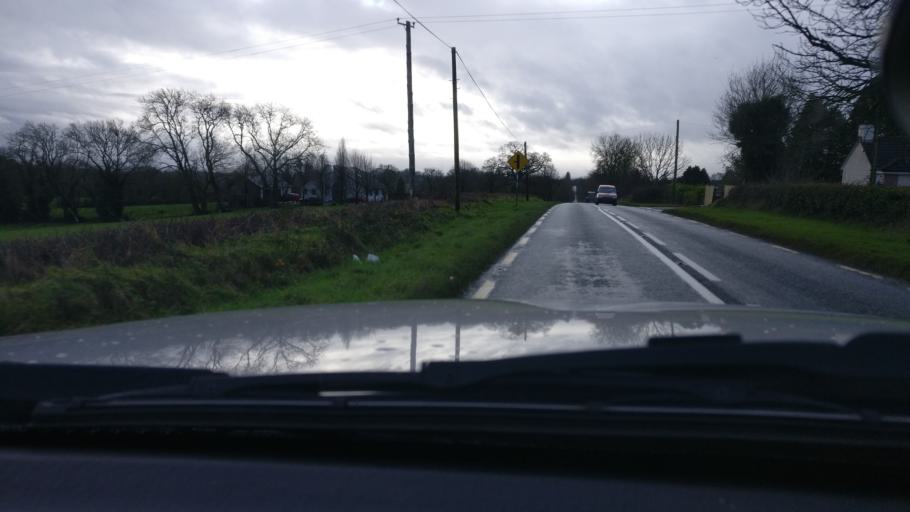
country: IE
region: Leinster
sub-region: An Iarmhi
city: Moate
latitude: 53.6256
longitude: -7.6961
